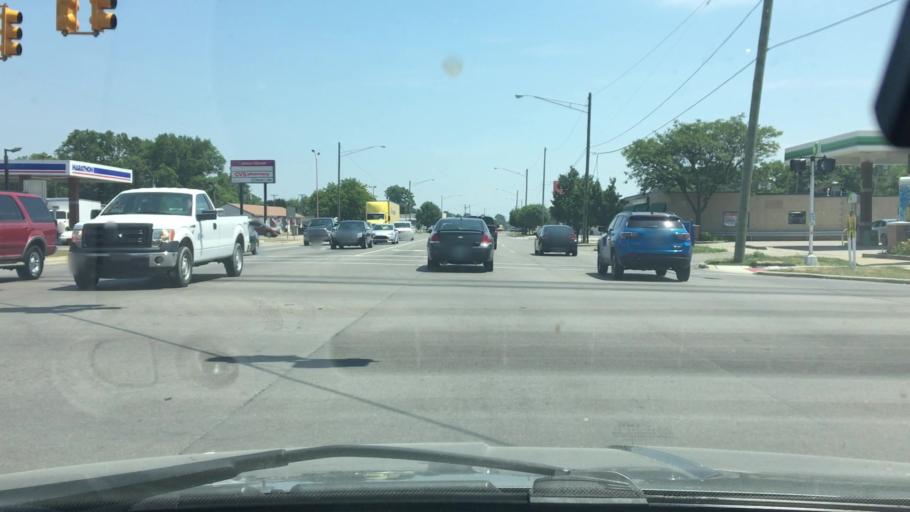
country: US
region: Michigan
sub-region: Wayne County
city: Redford
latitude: 42.3699
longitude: -83.3136
